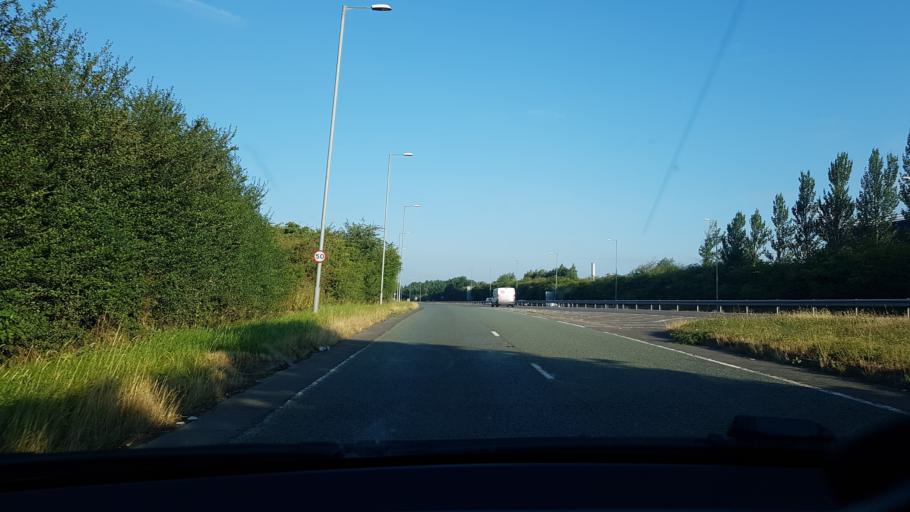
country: GB
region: England
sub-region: Nottinghamshire
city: Awsworth
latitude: 53.0007
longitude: -1.2836
